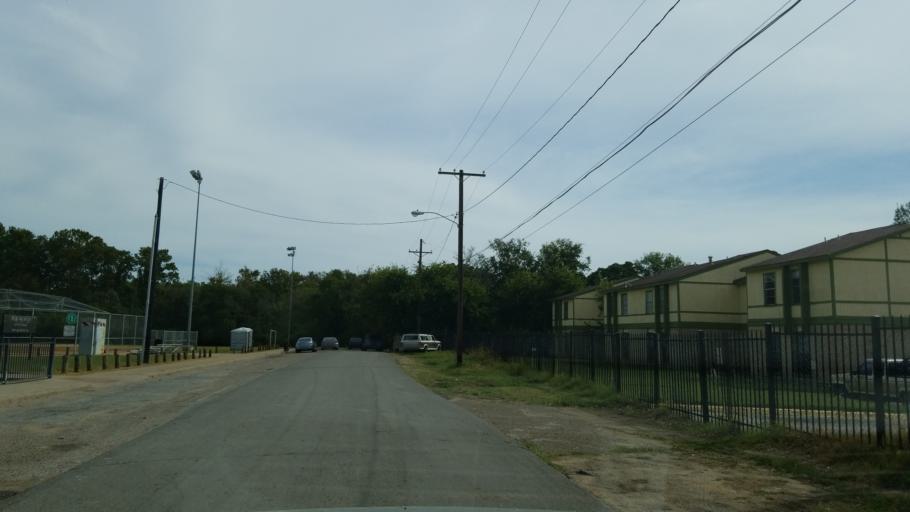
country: US
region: Texas
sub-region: Dallas County
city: Dallas
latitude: 32.7611
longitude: -96.7372
